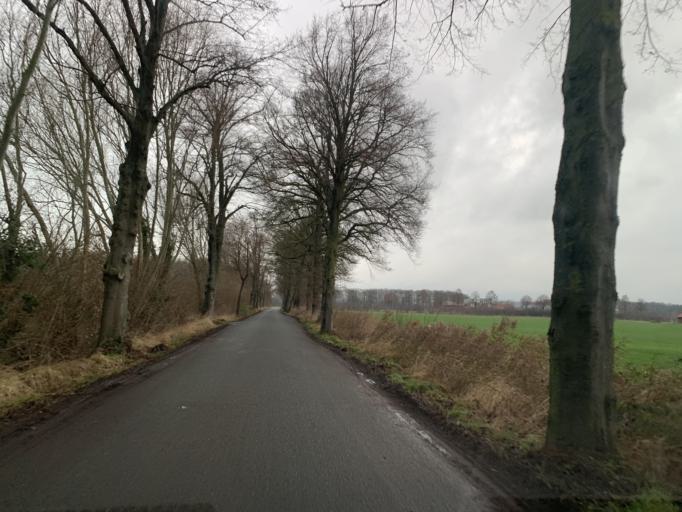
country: DE
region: North Rhine-Westphalia
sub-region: Regierungsbezirk Munster
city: Nordwalde
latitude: 52.0935
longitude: 7.5014
